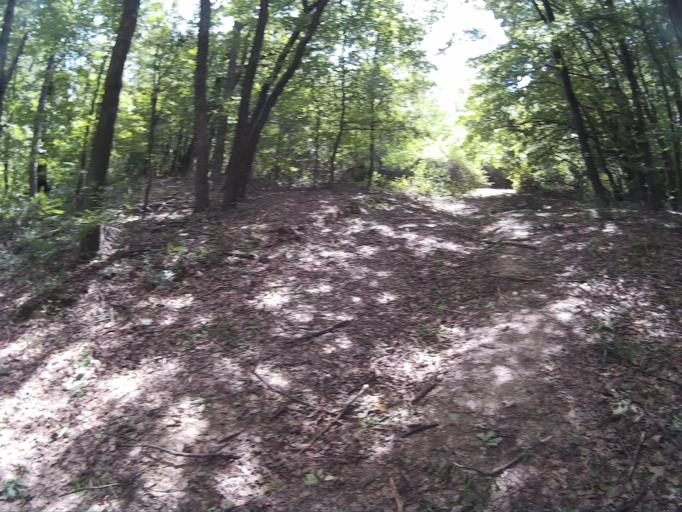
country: HU
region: Zala
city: Zalalovo
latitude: 46.8383
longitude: 16.5833
